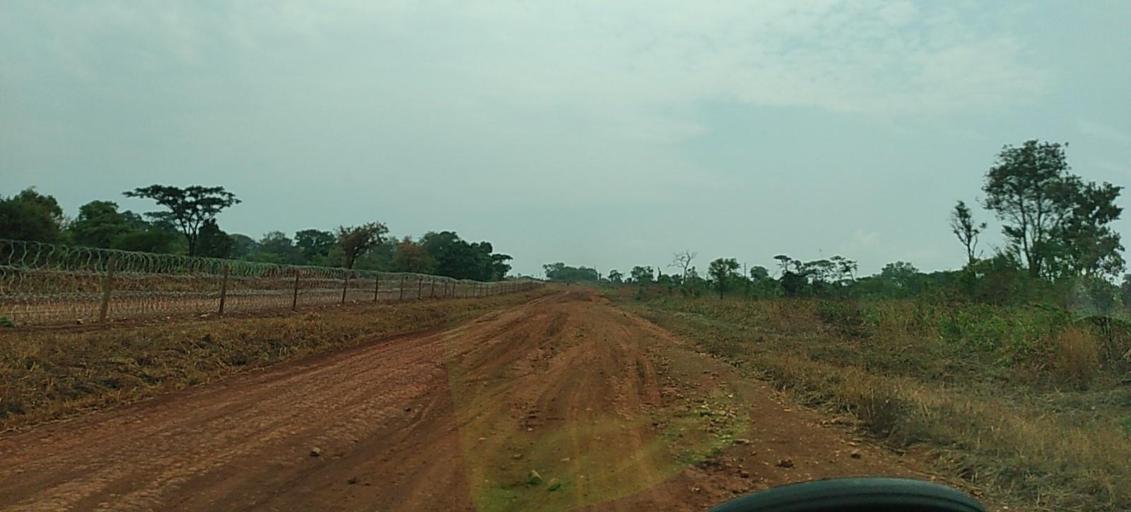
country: ZM
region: North-Western
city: Kansanshi
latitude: -12.0998
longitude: 26.4912
